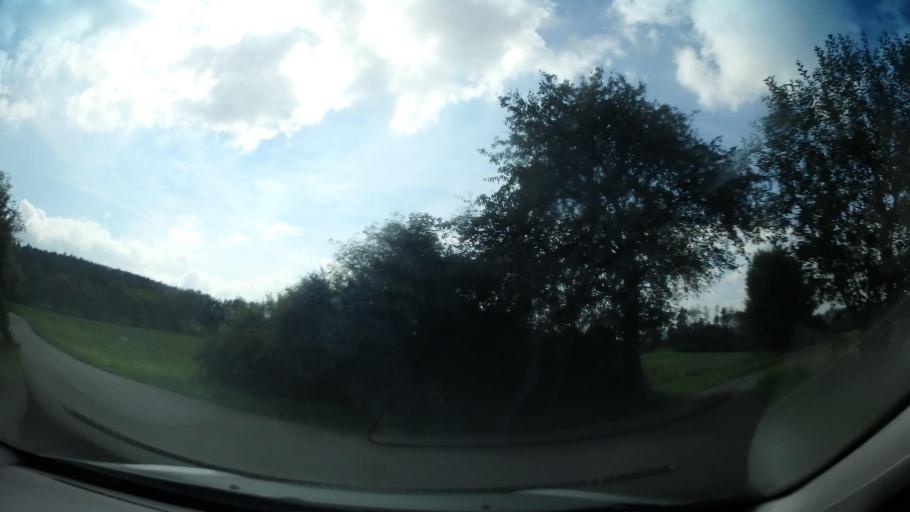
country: CZ
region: Central Bohemia
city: Novy Knin
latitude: 49.6985
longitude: 14.3196
